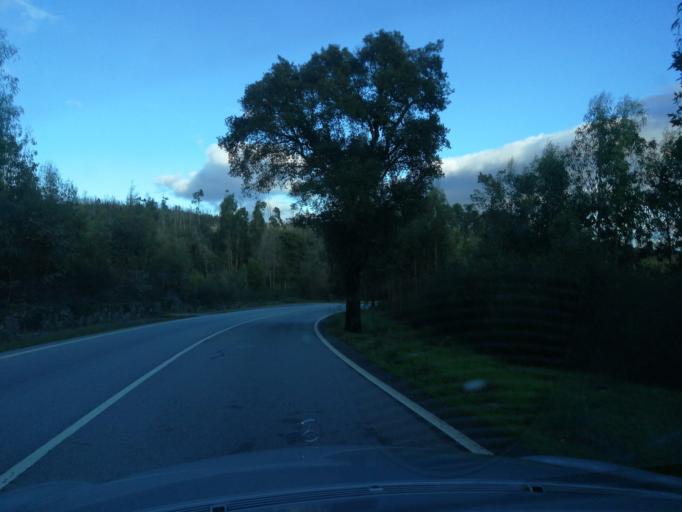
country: PT
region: Braga
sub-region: Barcelos
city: Vila Frescainha
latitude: 41.5666
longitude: -8.6677
